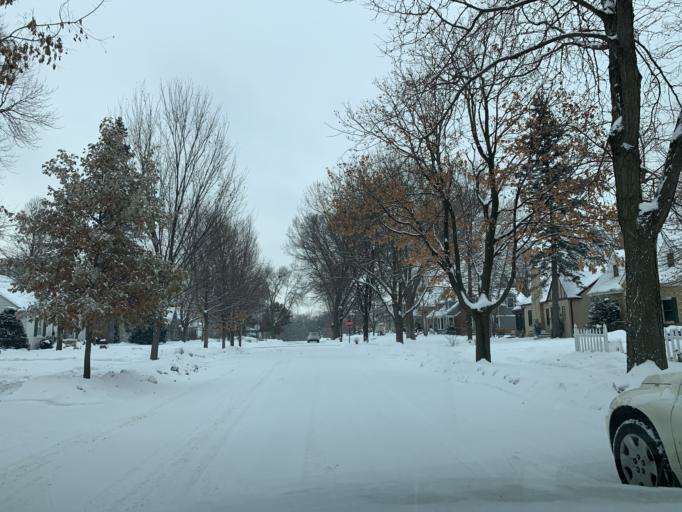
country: US
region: Minnesota
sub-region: Hennepin County
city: Saint Louis Park
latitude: 44.9312
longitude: -93.3367
